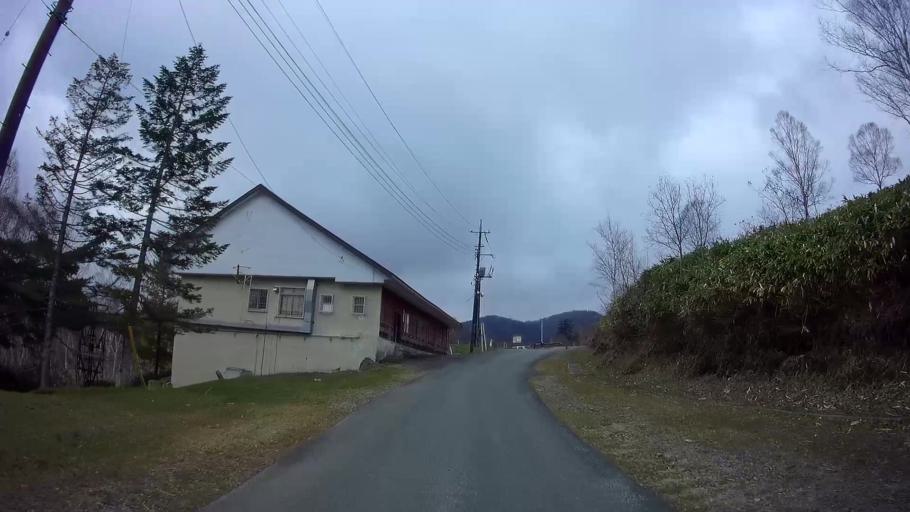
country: JP
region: Gunma
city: Nakanojomachi
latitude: 36.7172
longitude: 138.6401
